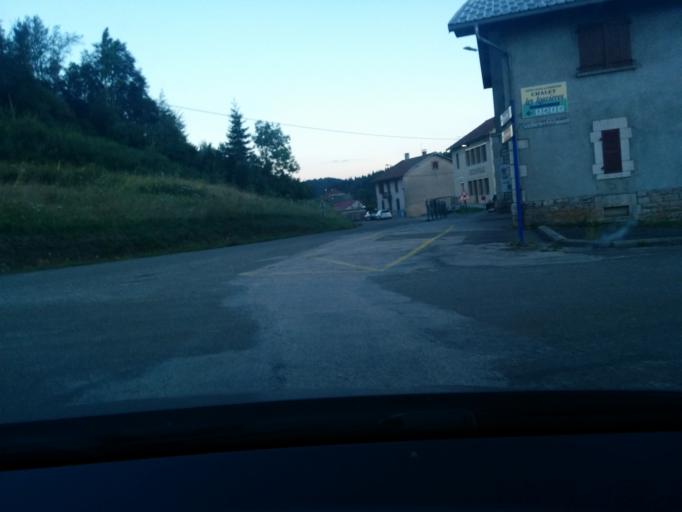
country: FR
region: Franche-Comte
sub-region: Departement du Jura
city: Saint-Lupicin
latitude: 46.4617
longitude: 5.7950
